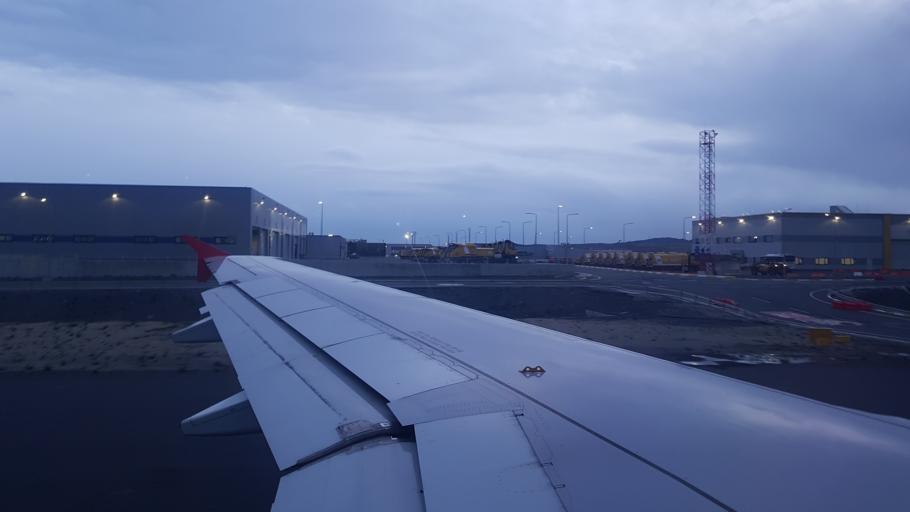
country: TR
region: Istanbul
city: Durusu
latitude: 41.2651
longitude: 28.7175
